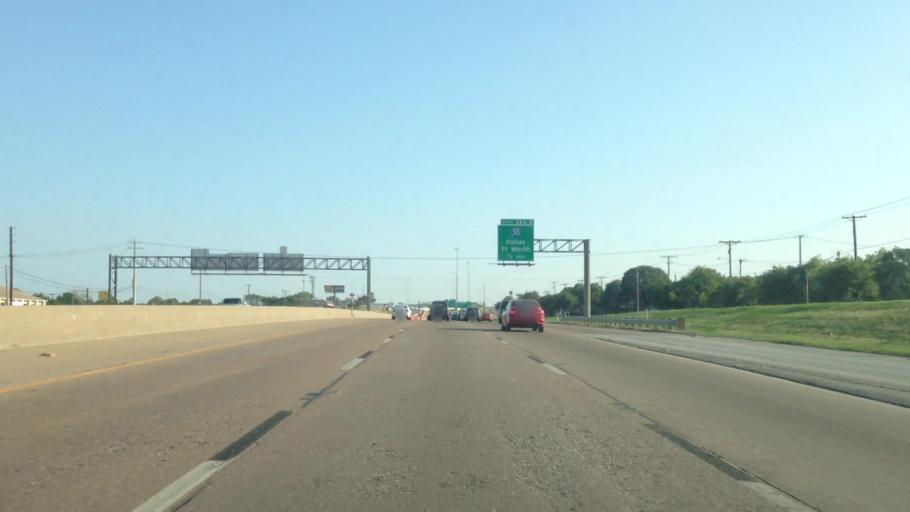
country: US
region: Texas
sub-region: Tarrant County
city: Richland Hills
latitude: 32.7761
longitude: -97.2128
